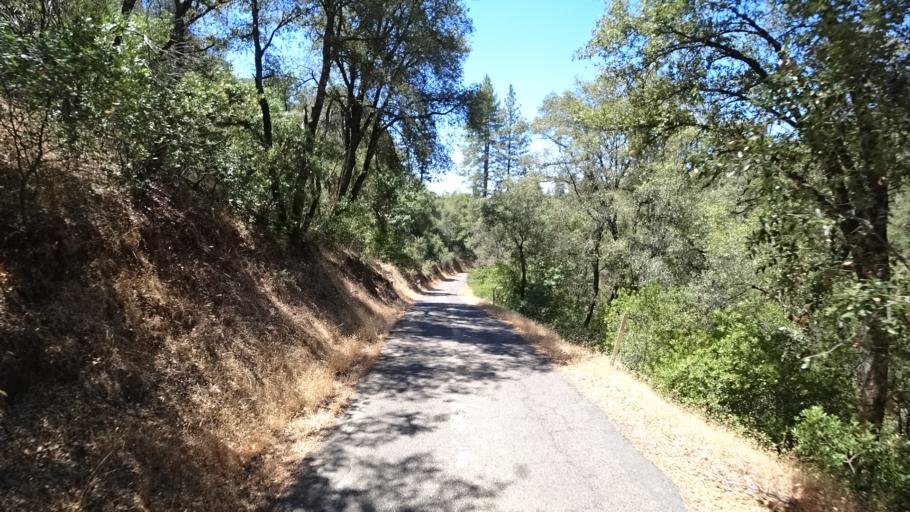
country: US
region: California
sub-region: Calaveras County
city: Murphys
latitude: 38.1372
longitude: -120.4272
